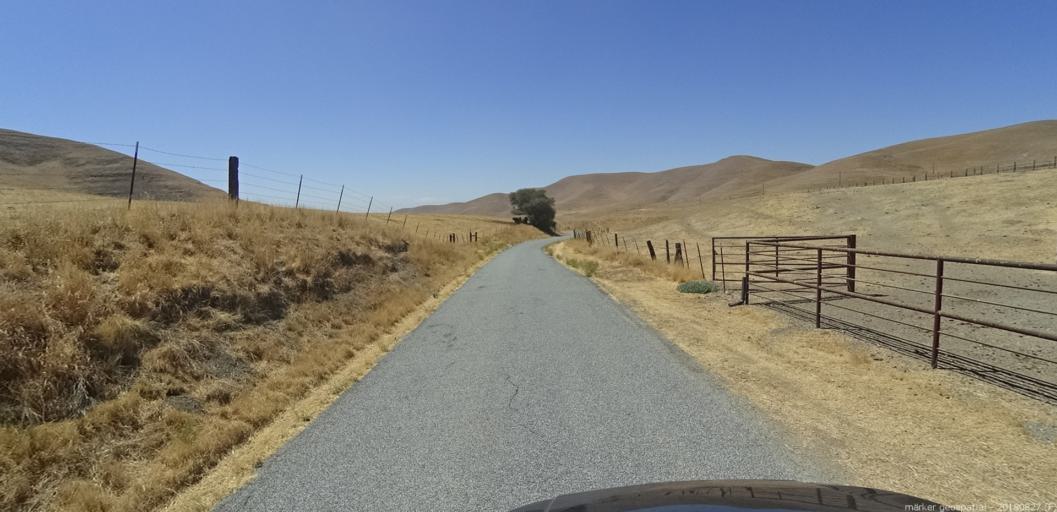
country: US
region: California
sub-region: Monterey County
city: King City
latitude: 36.1382
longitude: -120.8661
